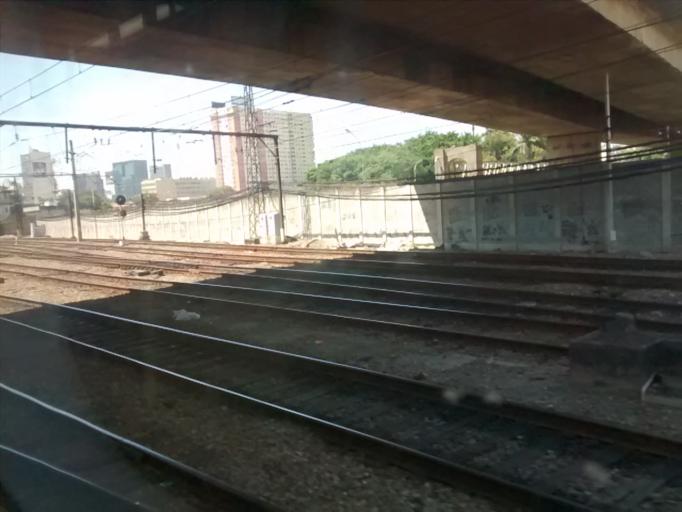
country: BR
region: Rio de Janeiro
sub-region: Rio De Janeiro
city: Rio de Janeiro
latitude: -22.9048
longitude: -43.1985
